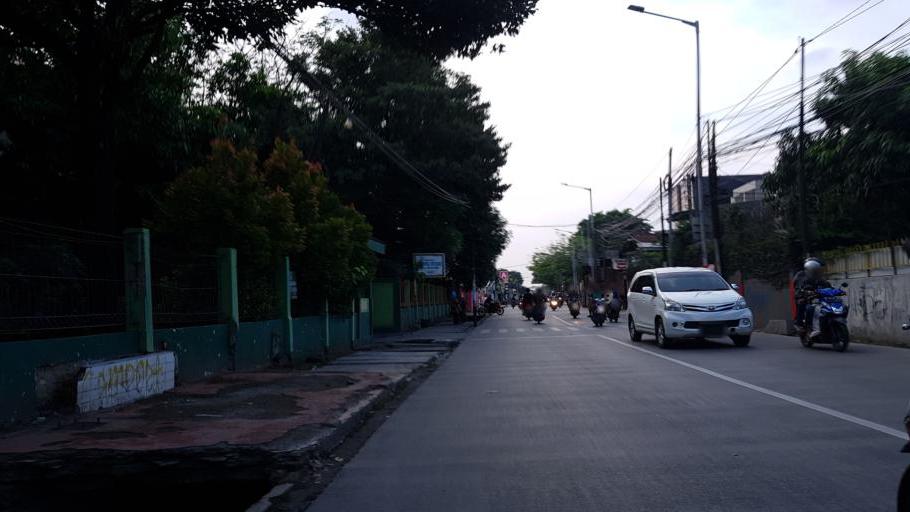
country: ID
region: West Java
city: Teluknaga
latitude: -6.1293
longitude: 106.7434
